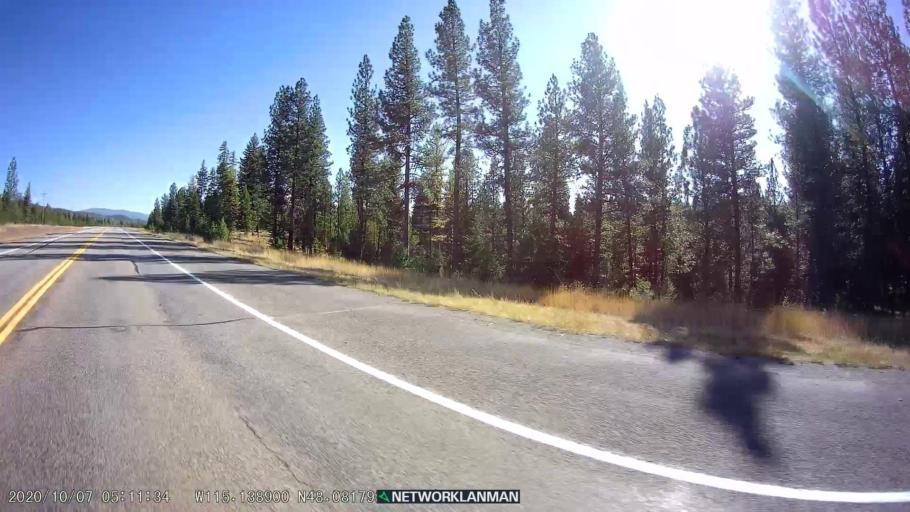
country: US
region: Montana
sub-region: Lincoln County
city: Libby
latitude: 48.0817
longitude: -115.1387
